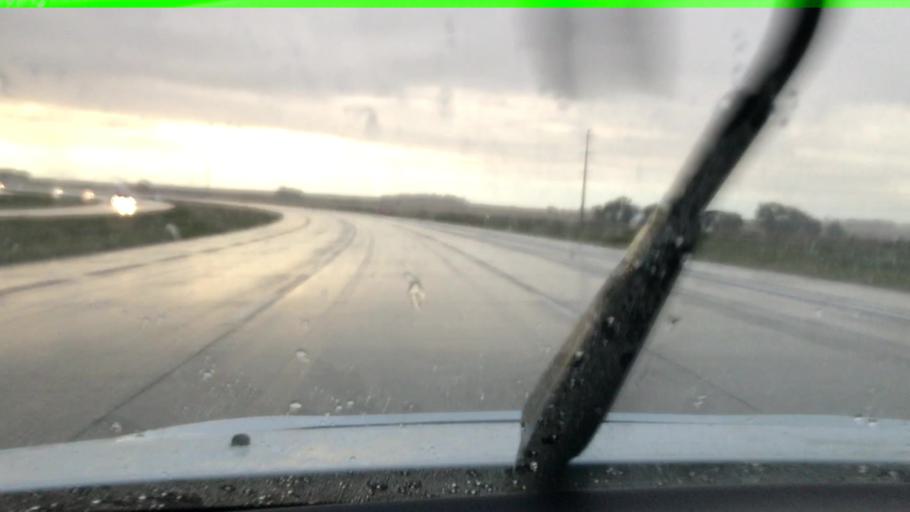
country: US
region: Nebraska
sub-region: Lancaster County
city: Waverly
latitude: 40.8940
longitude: -96.5631
